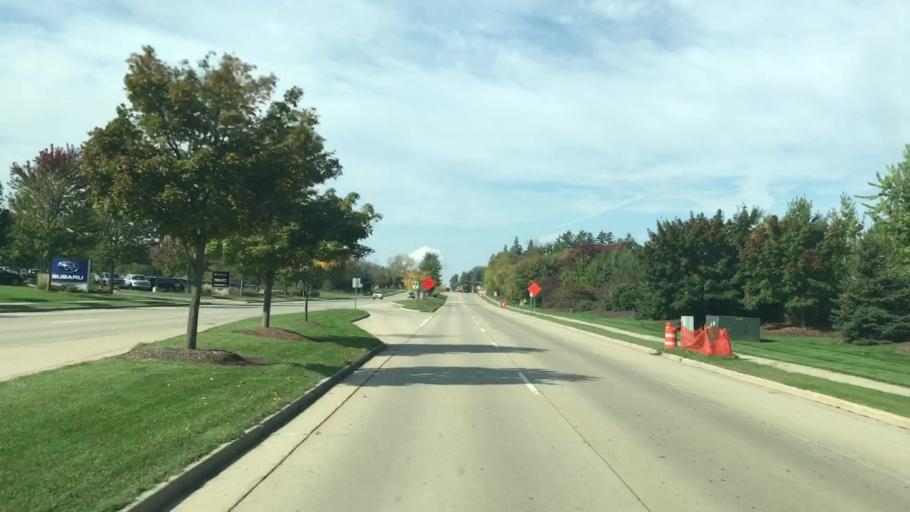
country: US
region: Wisconsin
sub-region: Ozaukee County
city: Mequon
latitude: 43.2217
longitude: -87.9983
